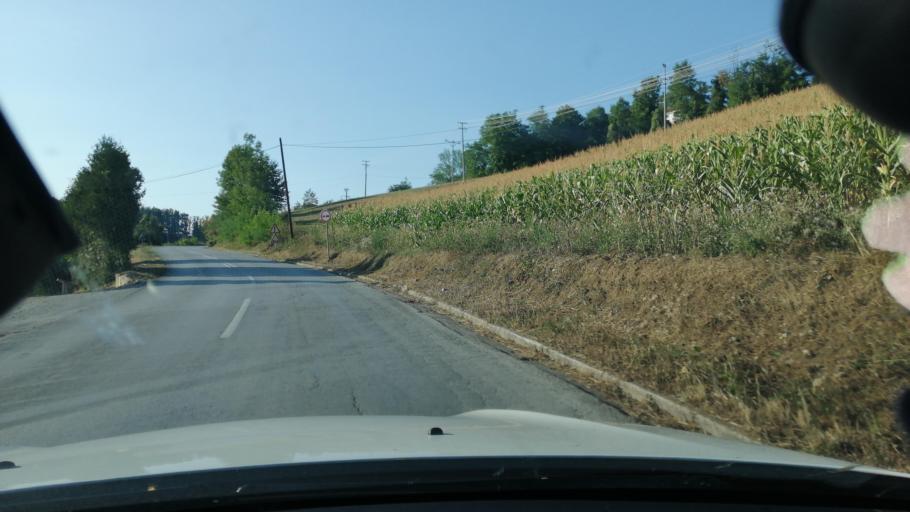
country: RS
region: Central Serbia
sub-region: Moravicki Okrug
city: Ivanjica
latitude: 43.6362
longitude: 20.2420
